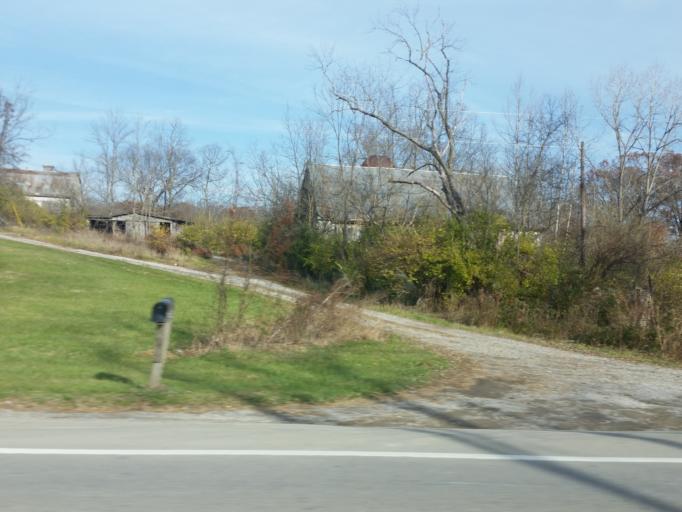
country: US
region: Kentucky
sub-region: Campbell County
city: Claryville
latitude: 38.8386
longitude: -84.3705
